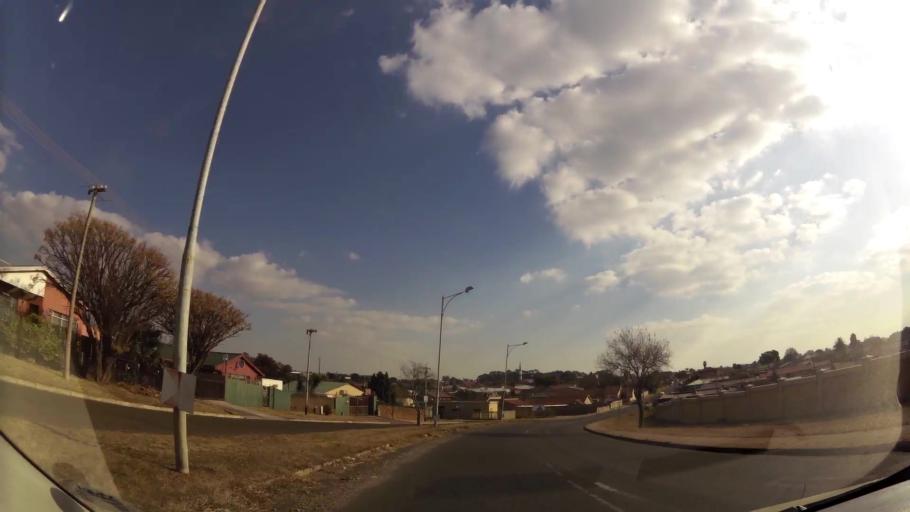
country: ZA
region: Gauteng
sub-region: West Rand District Municipality
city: Krugersdorp
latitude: -26.0929
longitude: 27.7544
